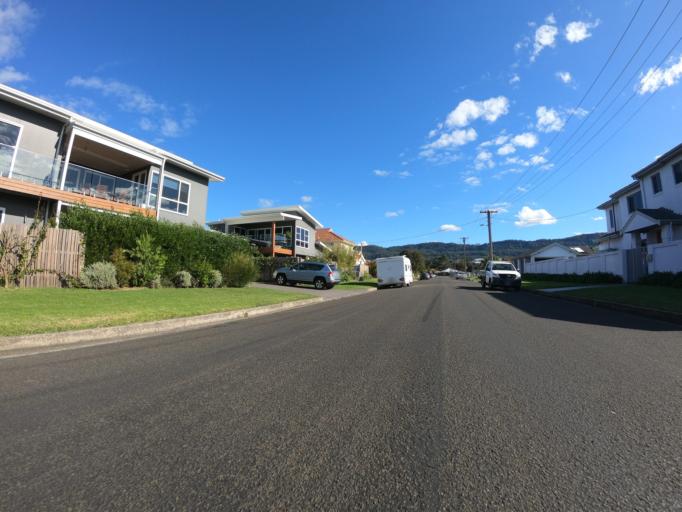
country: AU
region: New South Wales
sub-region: Wollongong
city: Bulli
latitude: -34.3517
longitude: 150.9188
